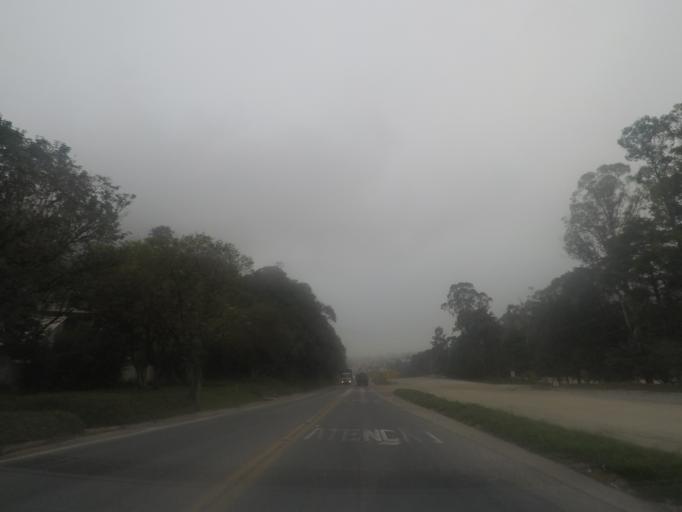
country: BR
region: Parana
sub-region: Almirante Tamandare
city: Almirante Tamandare
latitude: -25.2680
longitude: -49.3033
